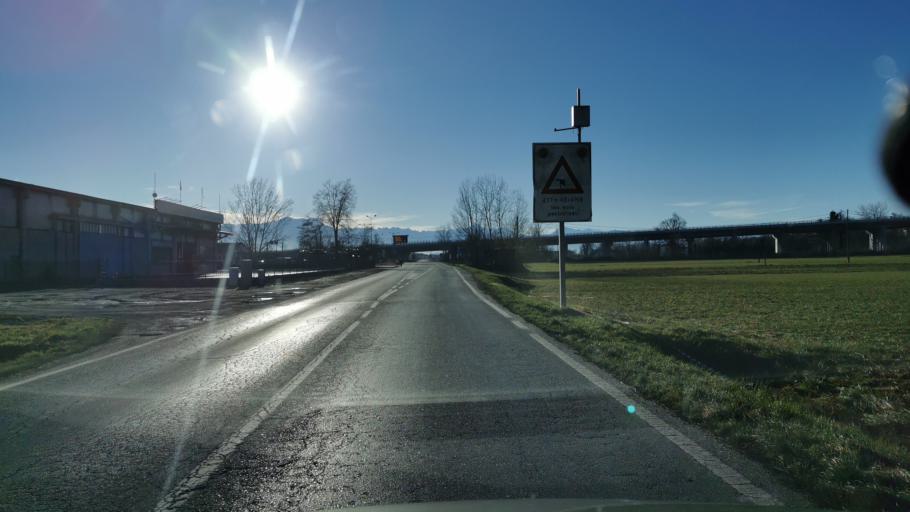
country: IT
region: Piedmont
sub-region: Provincia di Cuneo
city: Magliano Alpi
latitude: 44.4681
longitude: 7.8353
